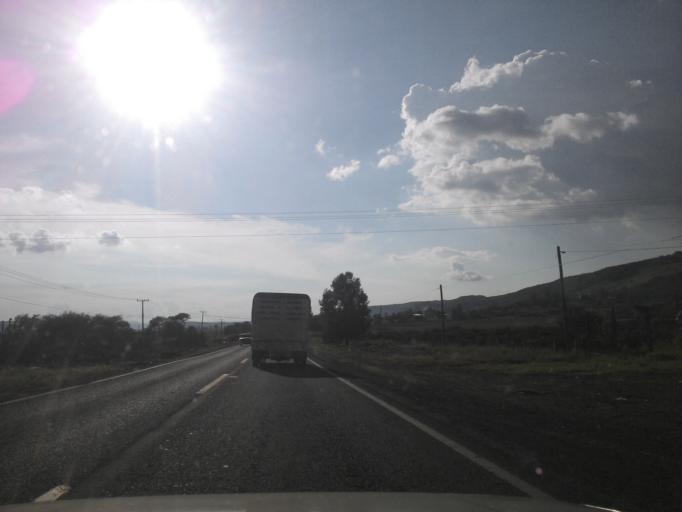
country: MX
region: Jalisco
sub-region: Atotonilco el Alto
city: Vistas del Maguey [Fraccionamiento]
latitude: 20.5410
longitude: -102.5680
